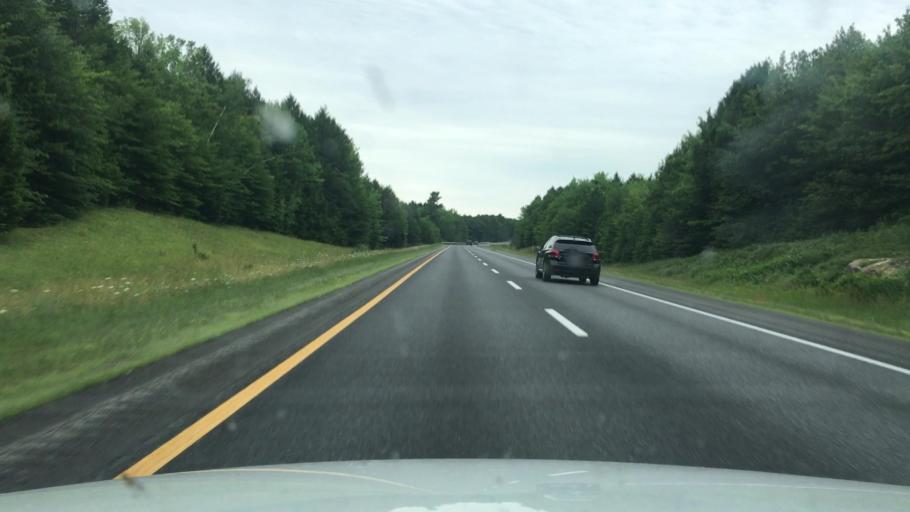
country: US
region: Maine
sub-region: Sagadahoc County
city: Richmond
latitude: 44.0486
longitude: -69.8944
